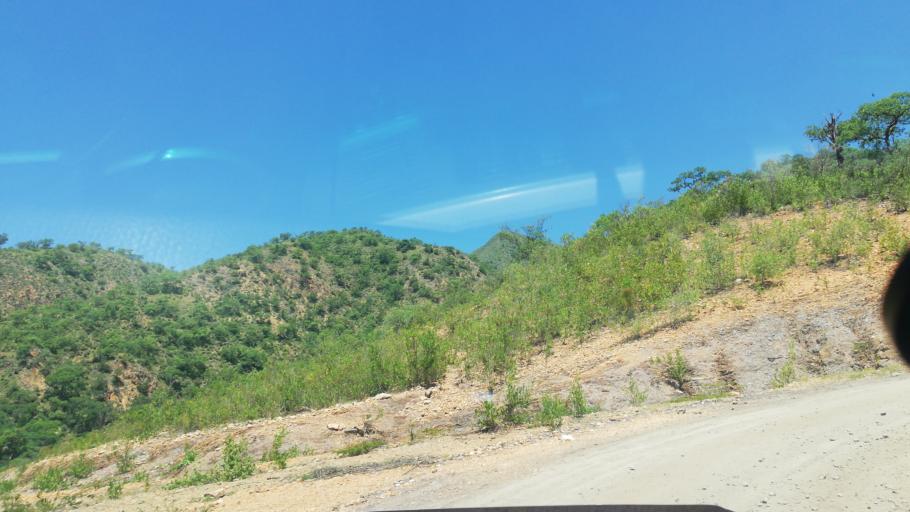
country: BO
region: Cochabamba
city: Mizque
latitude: -17.8787
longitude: -65.2896
